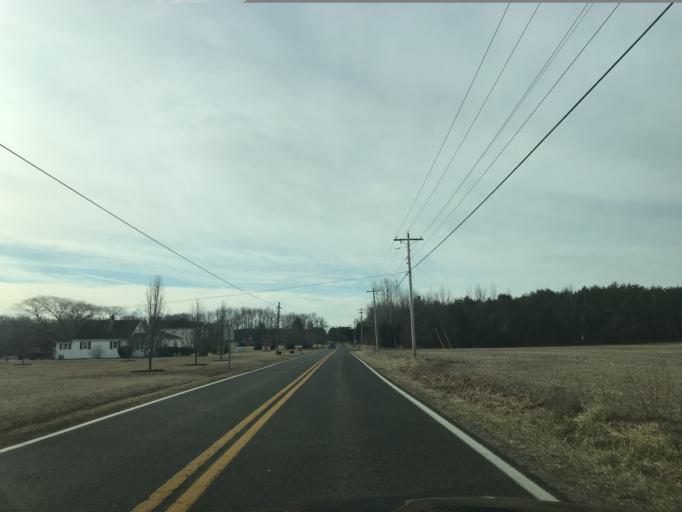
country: US
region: Maryland
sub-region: Charles County
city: Hughesville
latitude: 38.5305
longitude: -76.8418
